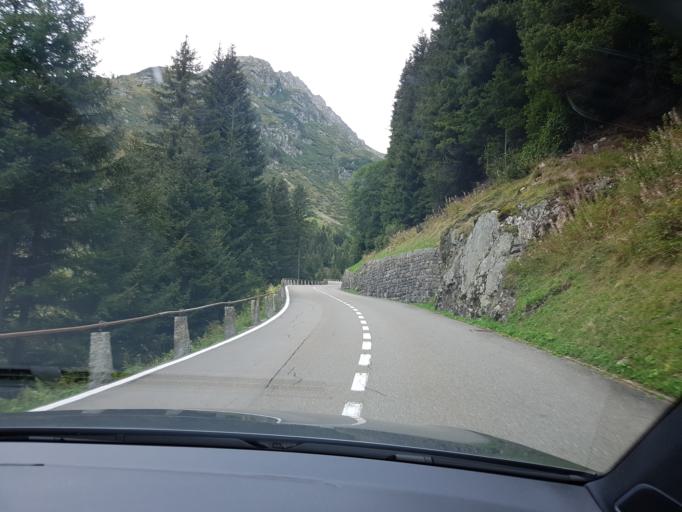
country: CH
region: Uri
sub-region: Uri
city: Andermatt
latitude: 46.7413
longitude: 8.5107
